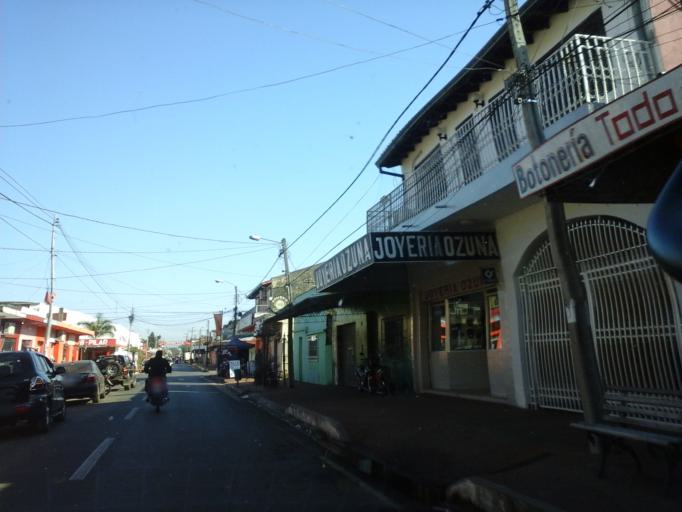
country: PY
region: Neembucu
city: Pilar
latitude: -26.8594
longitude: -58.3012
